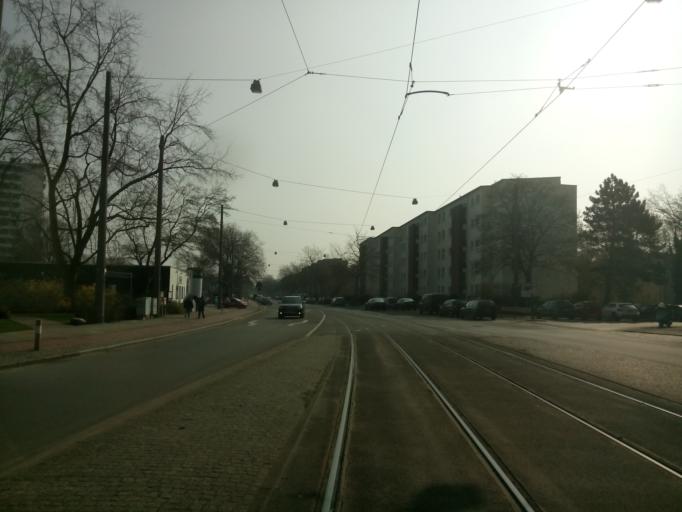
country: DE
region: Lower Saxony
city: Lilienthal
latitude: 53.0787
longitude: 8.9036
